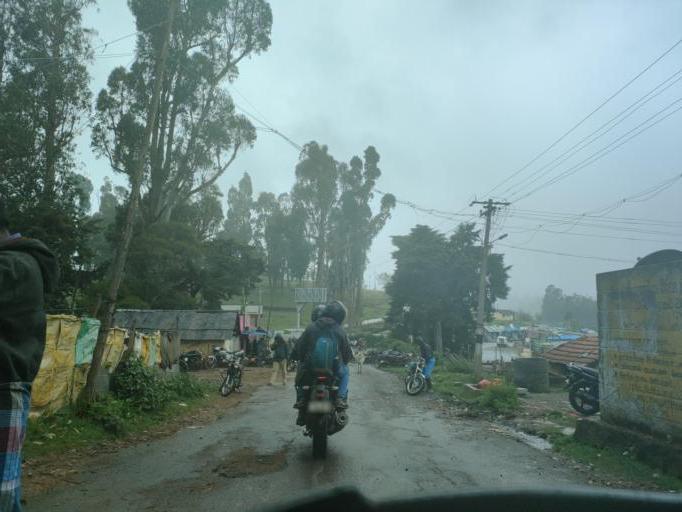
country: IN
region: Tamil Nadu
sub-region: Dindigul
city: Kodaikanal
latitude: 10.2286
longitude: 77.3512
